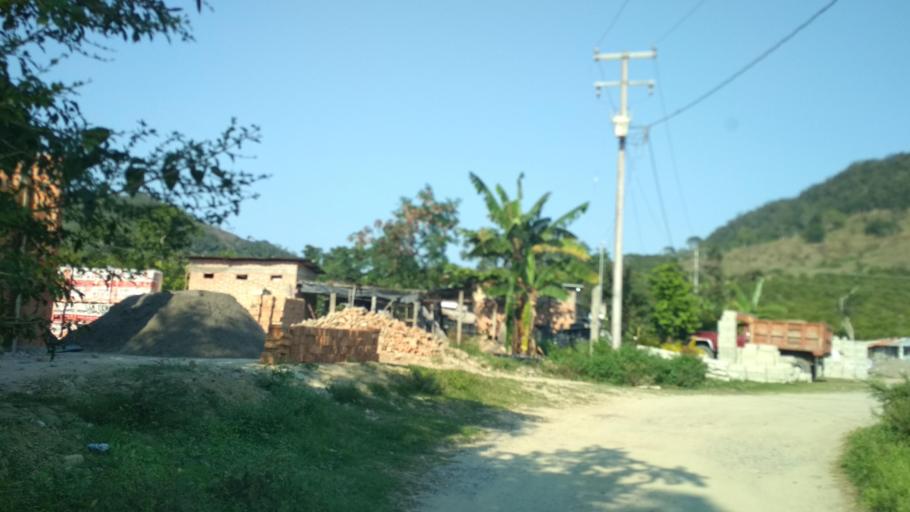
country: MM
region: Shan
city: Taunggyi
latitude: 20.4013
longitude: 97.3293
